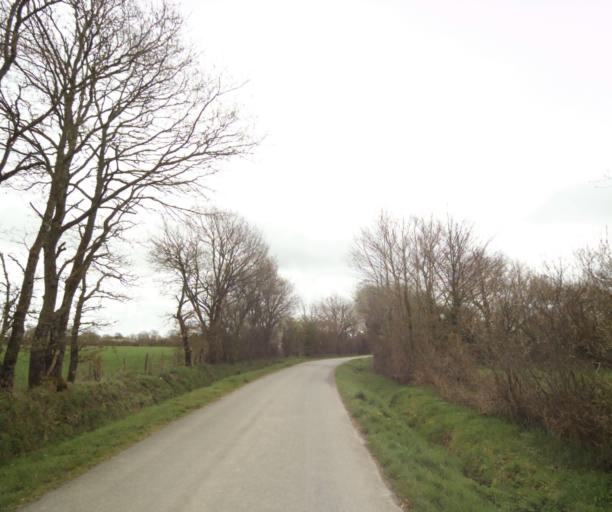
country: FR
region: Pays de la Loire
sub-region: Departement de la Loire-Atlantique
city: Bouvron
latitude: 47.4393
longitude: -1.8618
